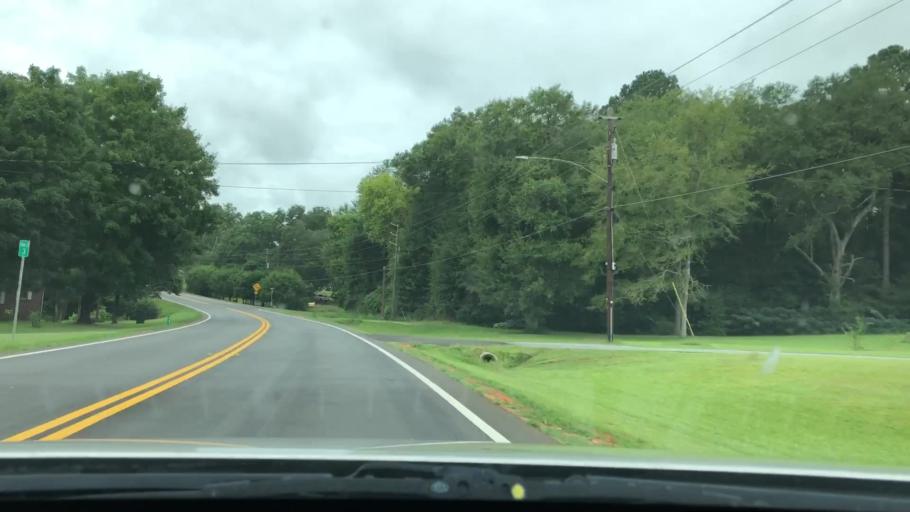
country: US
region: Georgia
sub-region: Upson County
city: Hannahs Mill
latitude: 33.0123
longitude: -84.4937
